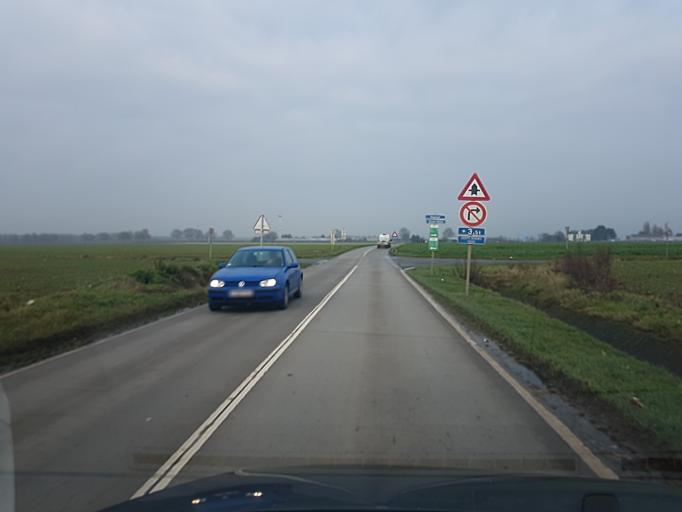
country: BE
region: Wallonia
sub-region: Province de Liege
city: Hannut
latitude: 50.6801
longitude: 5.0566
